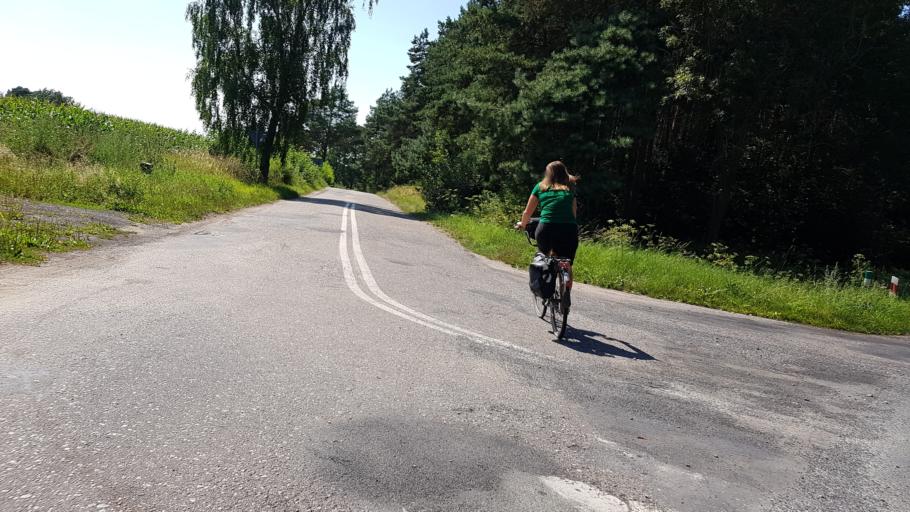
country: PL
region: West Pomeranian Voivodeship
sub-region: Powiat gryfinski
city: Gryfino
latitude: 53.1806
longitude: 14.5538
